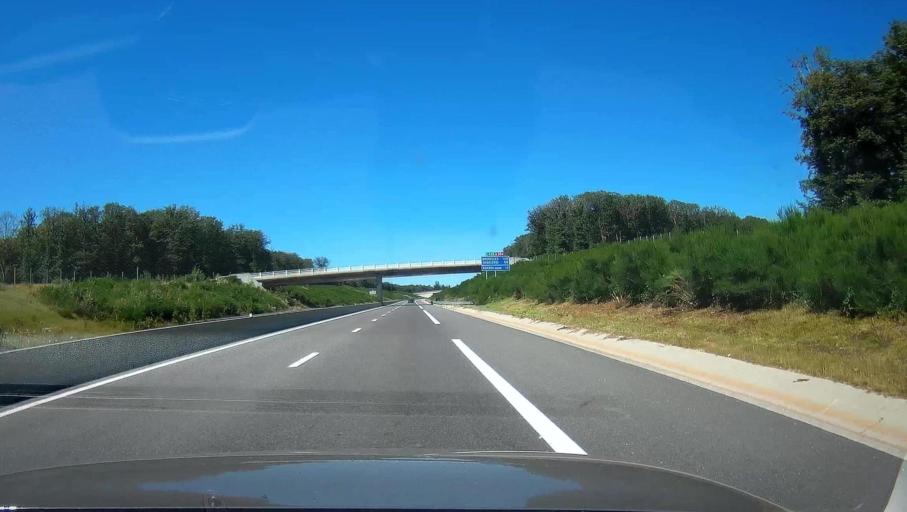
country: FR
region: Champagne-Ardenne
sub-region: Departement des Ardennes
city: Rimogne
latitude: 49.8561
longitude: 4.5120
